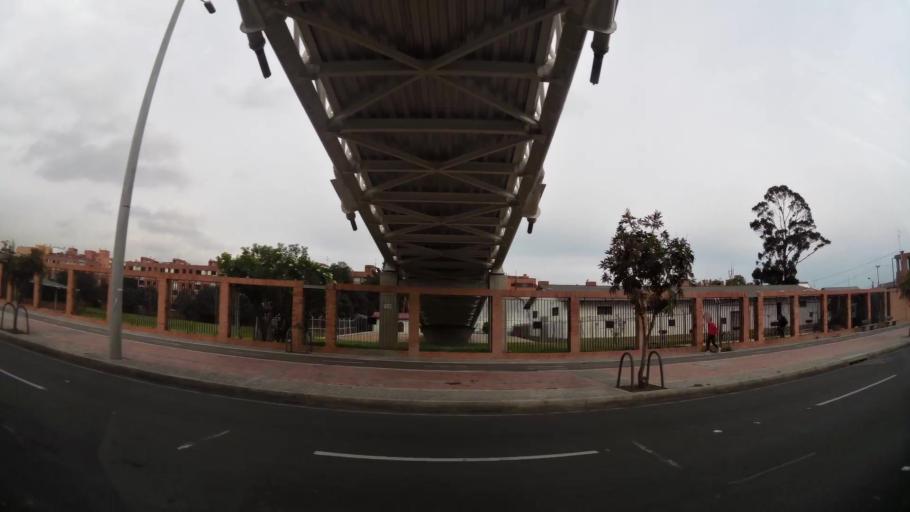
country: CO
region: Bogota D.C.
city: Barrio San Luis
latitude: 4.6851
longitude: -74.0422
